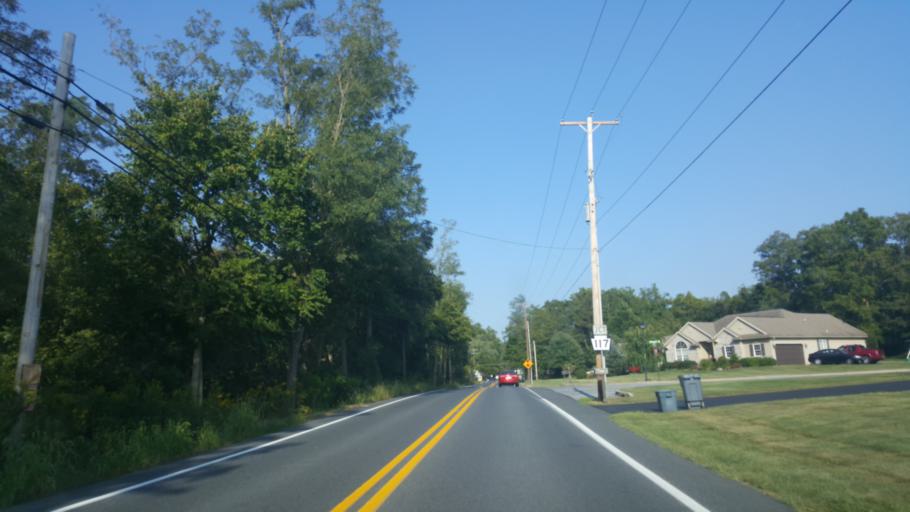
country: US
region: Pennsylvania
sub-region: Lebanon County
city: Campbelltown
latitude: 40.2395
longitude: -76.5153
